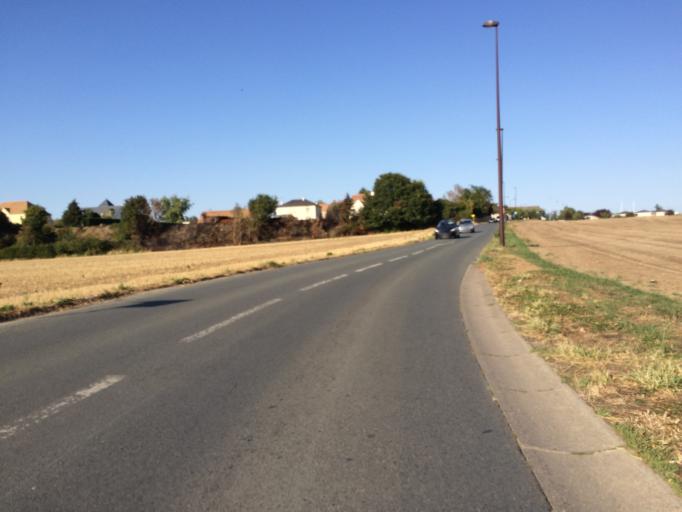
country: FR
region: Ile-de-France
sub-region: Departement de l'Essonne
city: Epinay-sur-Orge
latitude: 48.6714
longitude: 2.3096
